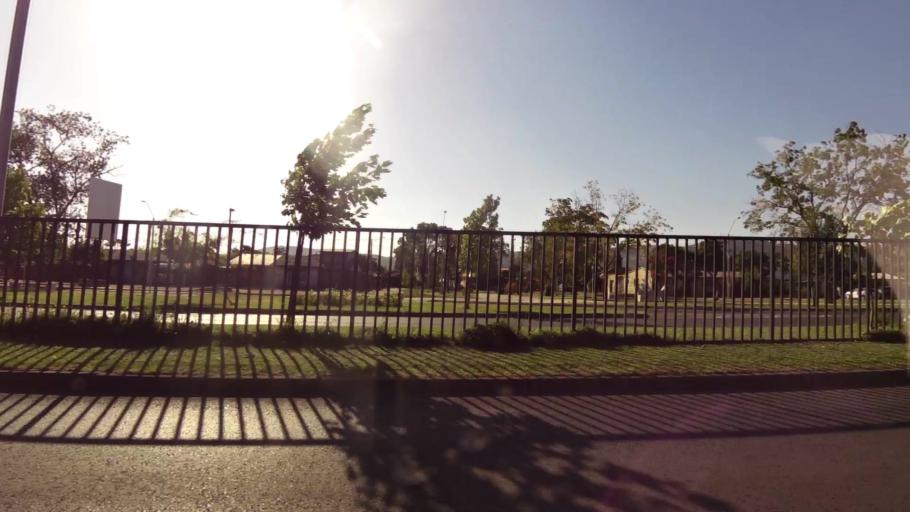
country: CL
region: Maule
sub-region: Provincia de Talca
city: Talca
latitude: -35.4376
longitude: -71.6815
